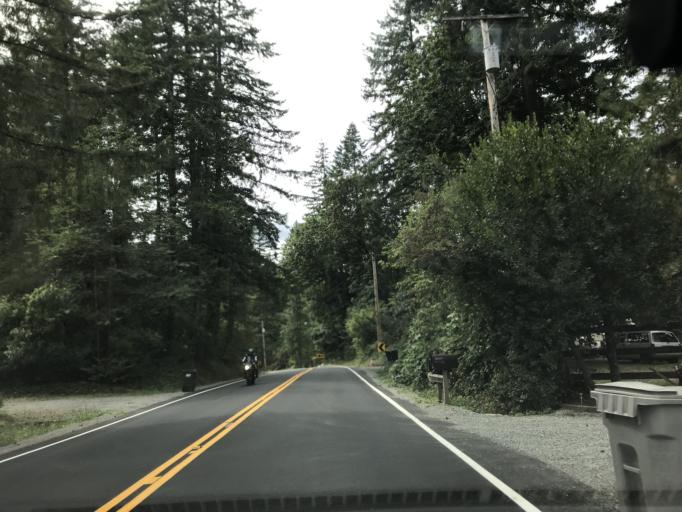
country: US
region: Washington
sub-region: King County
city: Black Diamond
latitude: 47.2867
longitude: -122.0200
